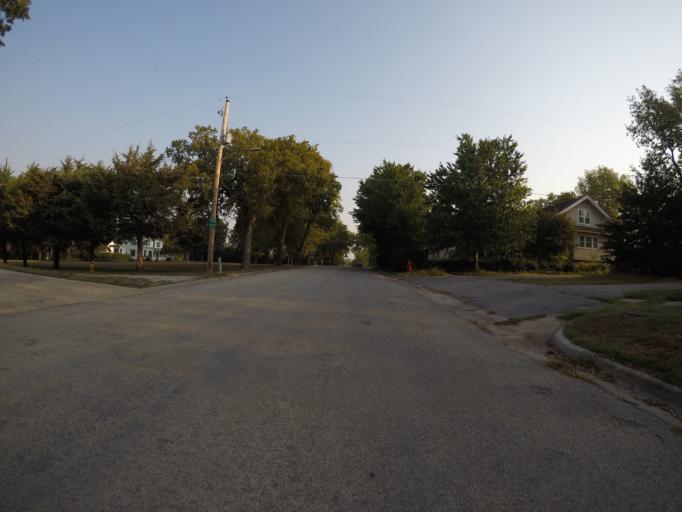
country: US
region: Kansas
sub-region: Marshall County
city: Marysville
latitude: 39.8519
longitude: -96.6480
